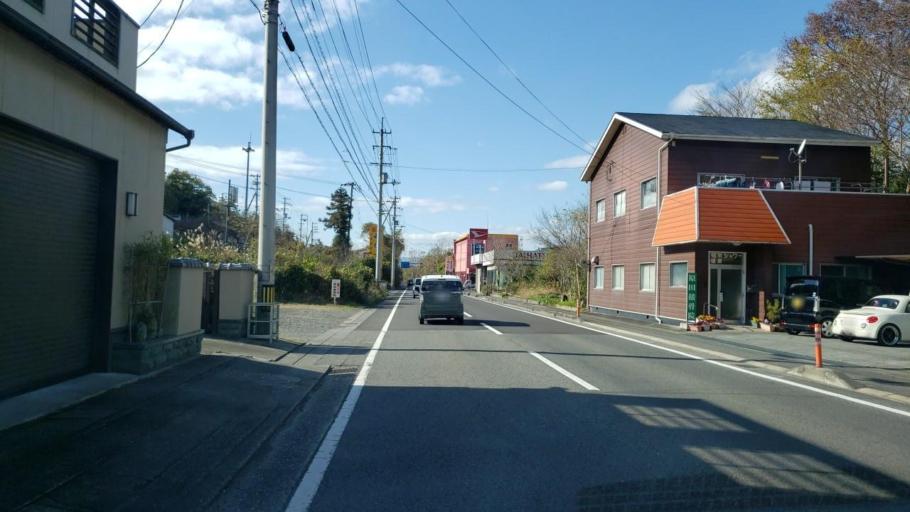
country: JP
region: Tokushima
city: Wakimachi
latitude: 34.0427
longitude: 134.0492
